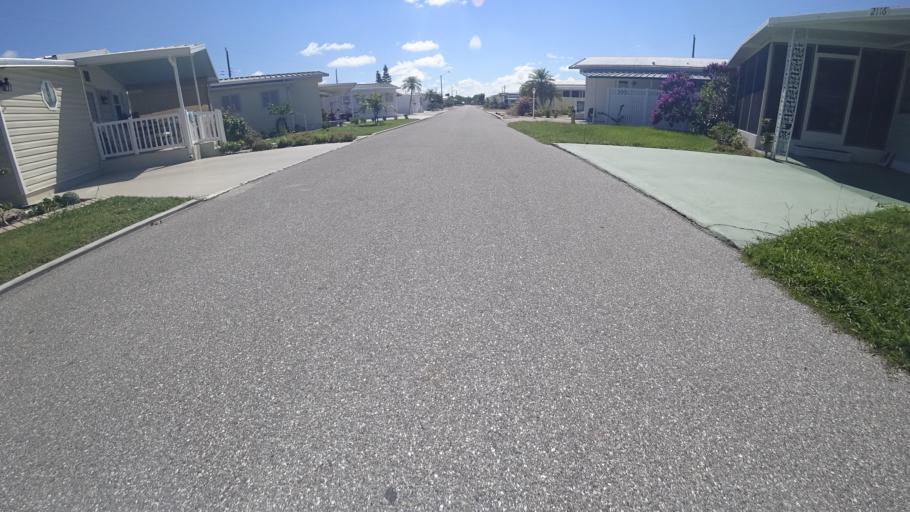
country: US
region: Florida
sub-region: Manatee County
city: Bayshore Gardens
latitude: 27.4214
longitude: -82.5836
